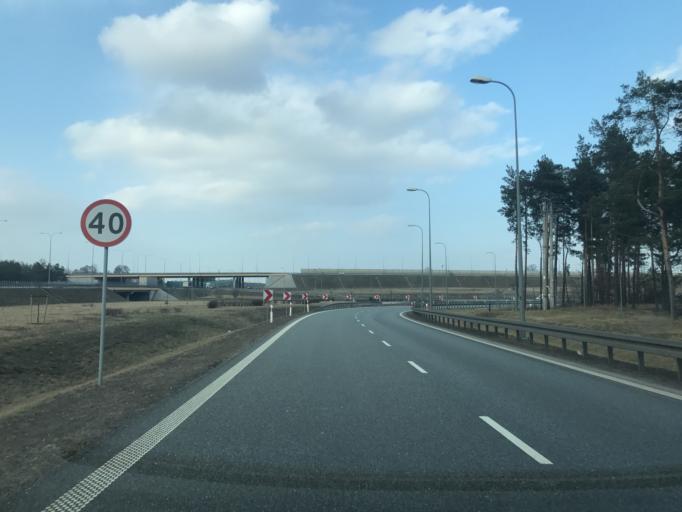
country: PL
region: Kujawsko-Pomorskie
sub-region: Powiat torunski
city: Lubicz Dolny
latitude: 53.0354
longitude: 18.7327
